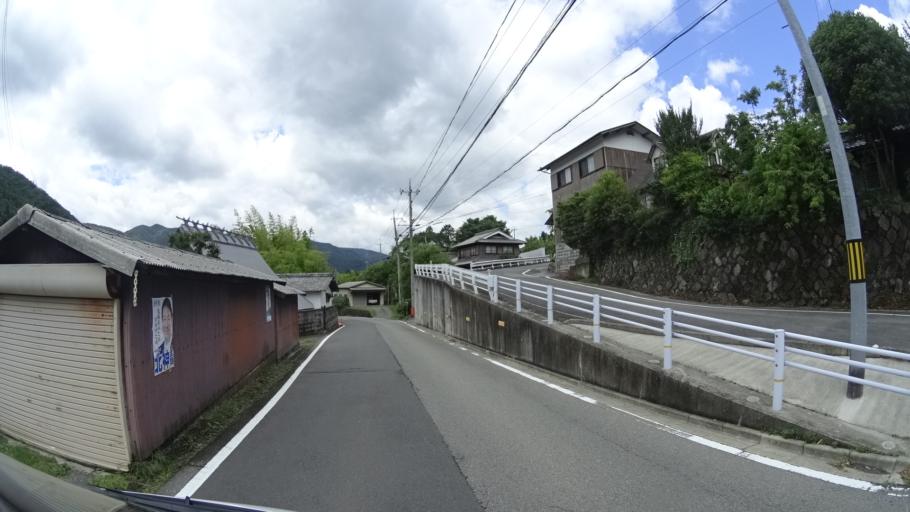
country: JP
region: Kyoto
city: Kameoka
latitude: 35.0135
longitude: 135.4442
